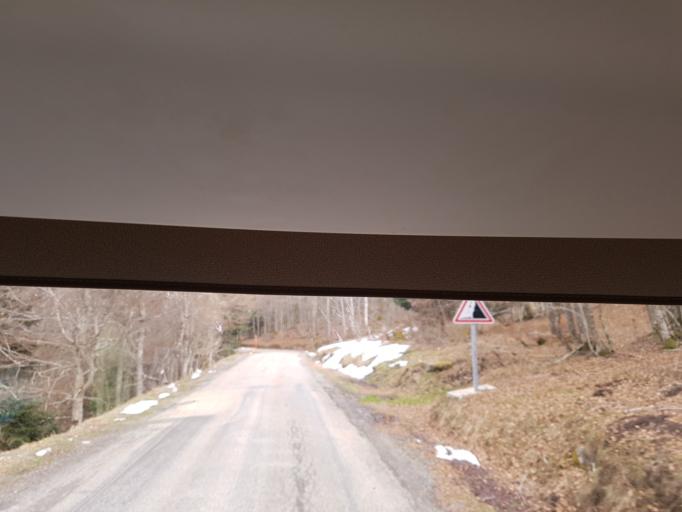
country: FR
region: Languedoc-Roussillon
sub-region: Departement de l'Aude
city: Quillan
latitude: 42.6766
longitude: 2.1339
